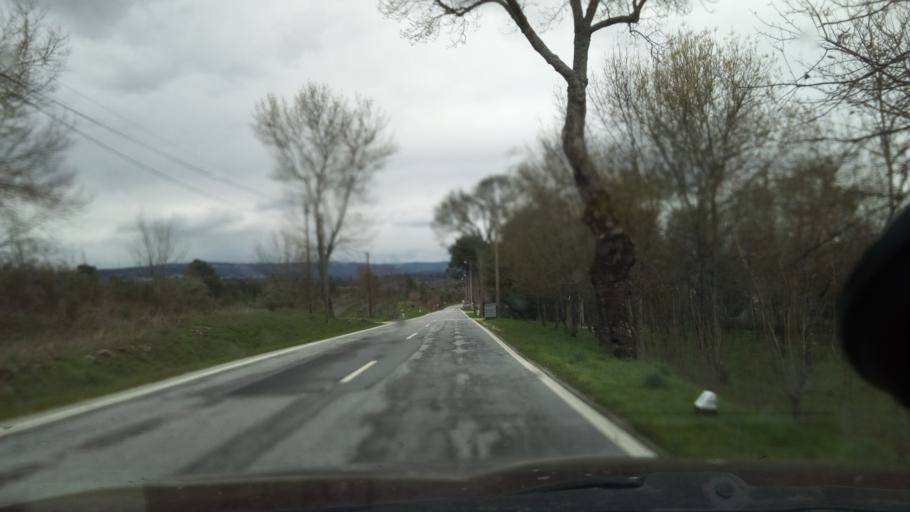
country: PT
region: Guarda
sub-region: Fornos de Algodres
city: Fornos de Algodres
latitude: 40.5431
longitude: -7.5350
